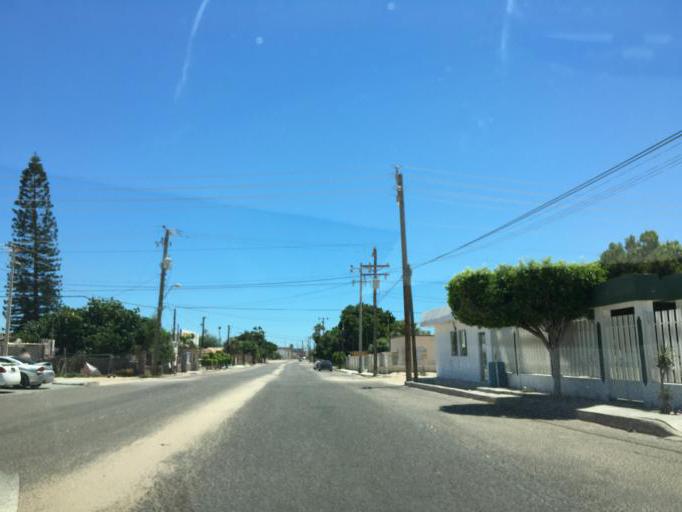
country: MX
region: Sonora
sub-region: Puerto Penasco
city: Puerto Penasco
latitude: 31.3103
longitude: -113.5336
